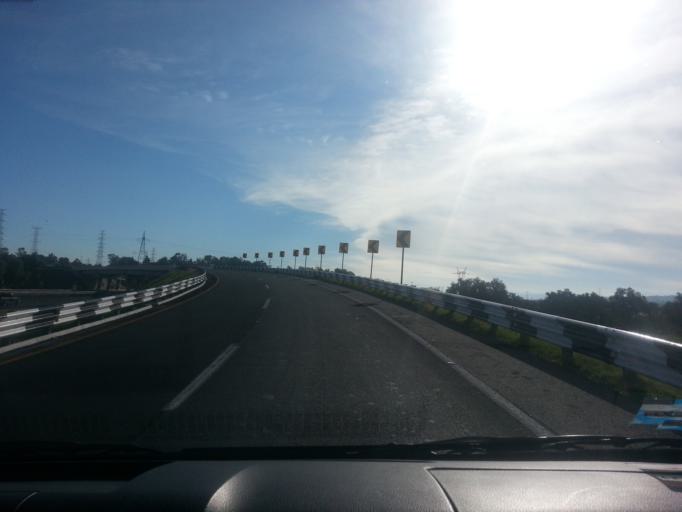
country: MX
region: Morelos
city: Xometla
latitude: 19.6547
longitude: -98.8791
